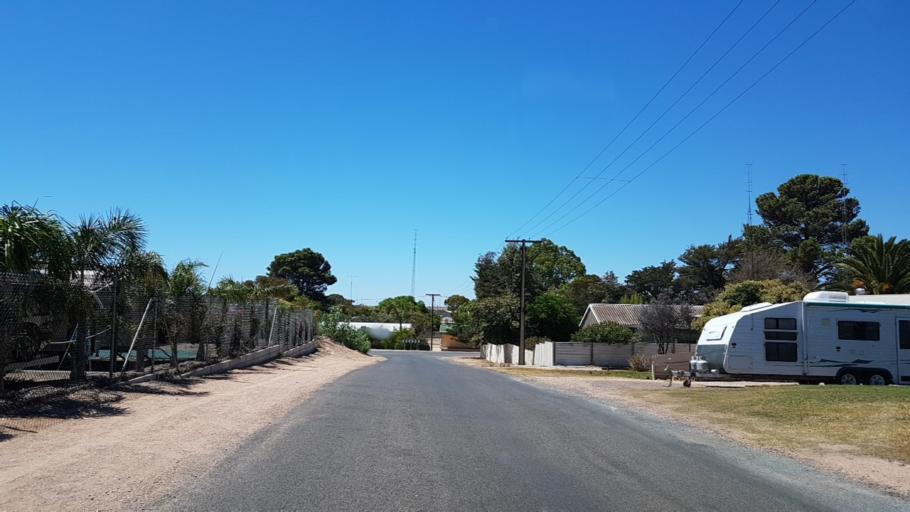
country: AU
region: South Australia
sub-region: Copper Coast
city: Wallaroo
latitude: -34.0533
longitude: 137.5649
